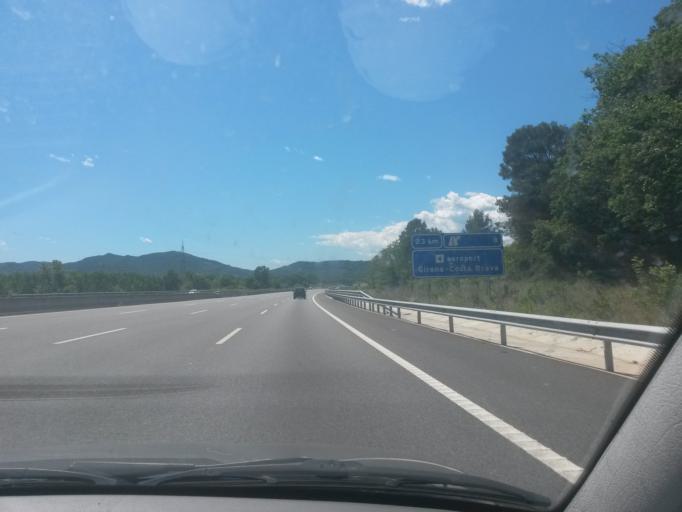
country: ES
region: Catalonia
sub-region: Provincia de Girona
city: Celra
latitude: 42.0565
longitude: 2.8817
